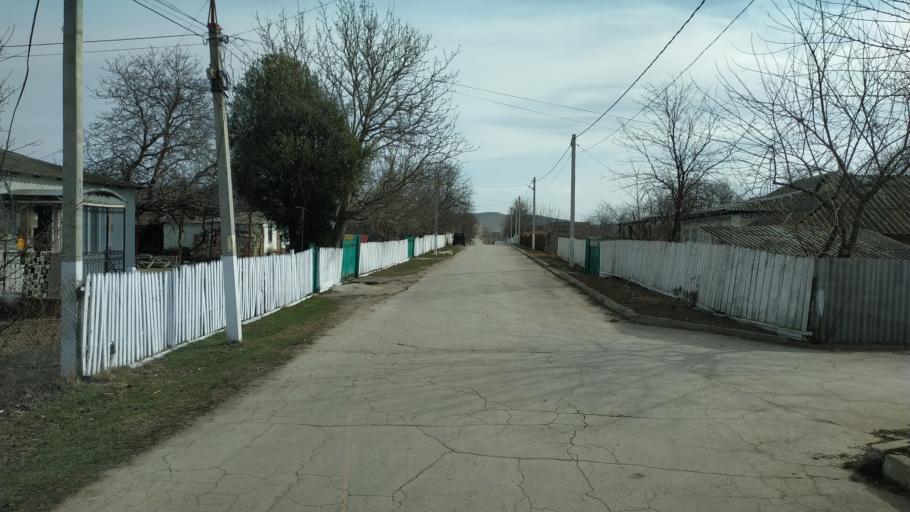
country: RO
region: Vaslui
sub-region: Comuna Dranceni
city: Dranceni
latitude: 46.8724
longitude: 28.2067
